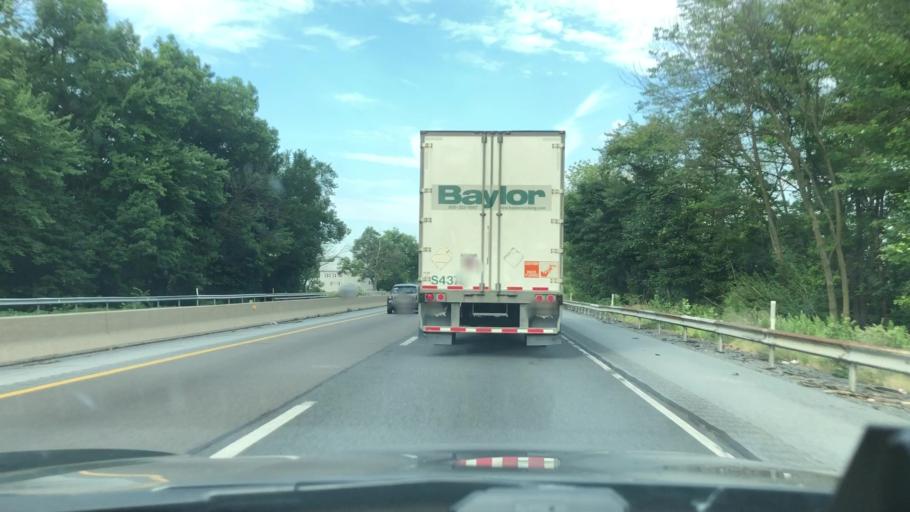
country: US
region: Pennsylvania
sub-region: Schuylkill County
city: Lake Wynonah
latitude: 40.4955
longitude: -76.2048
